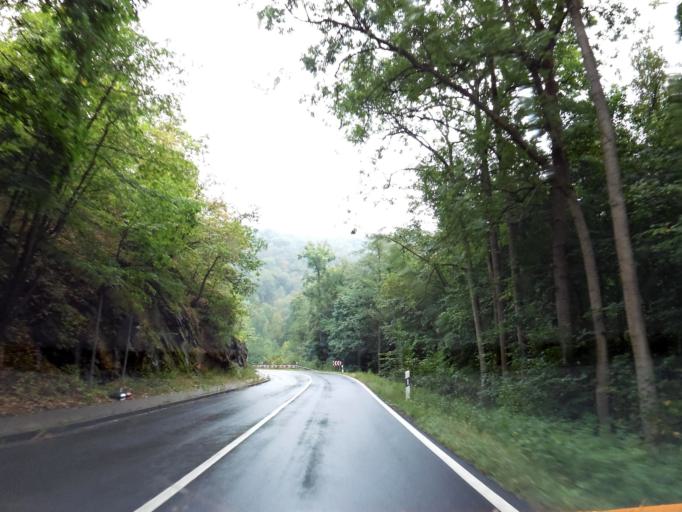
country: DE
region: Saxony-Anhalt
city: Harzgerode
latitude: 51.6669
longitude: 11.1297
